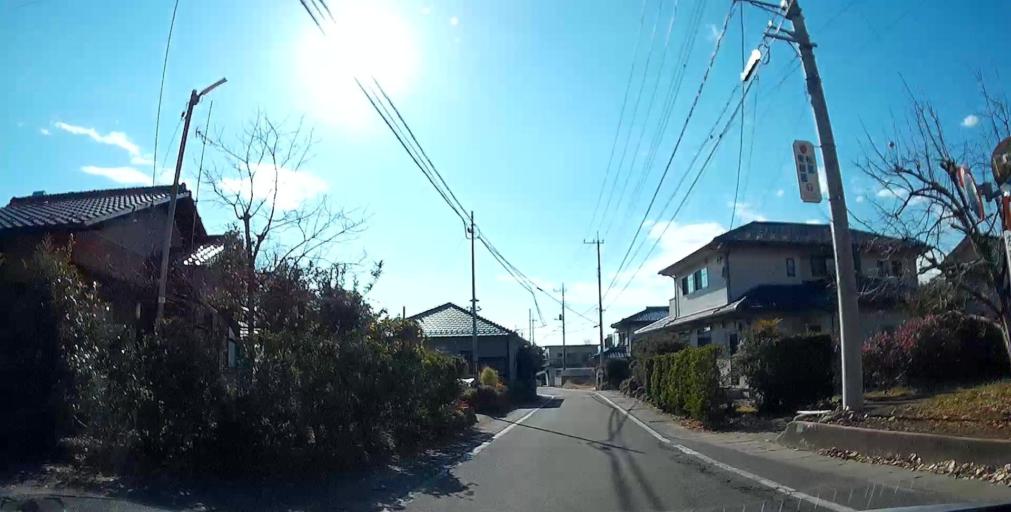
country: JP
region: Yamanashi
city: Enzan
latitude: 35.7332
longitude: 138.7181
